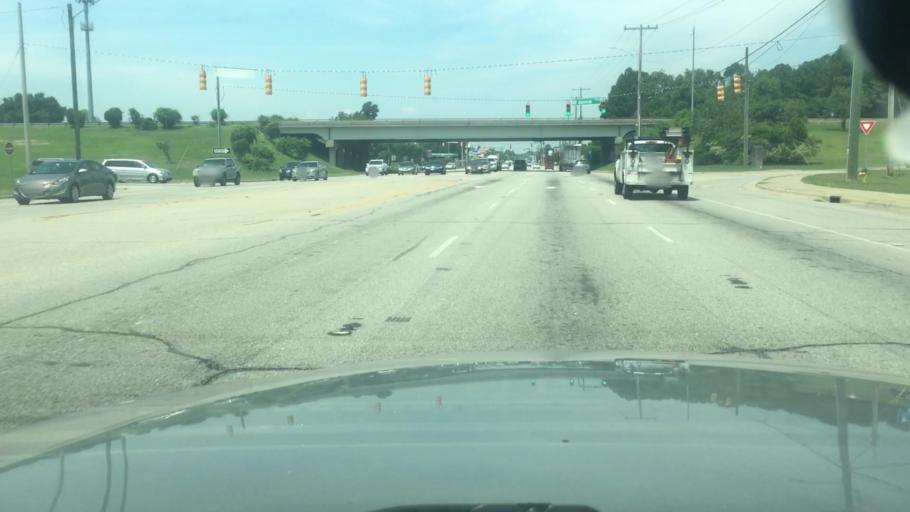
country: US
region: North Carolina
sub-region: Cumberland County
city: Fayetteville
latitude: 35.0443
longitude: -78.9378
